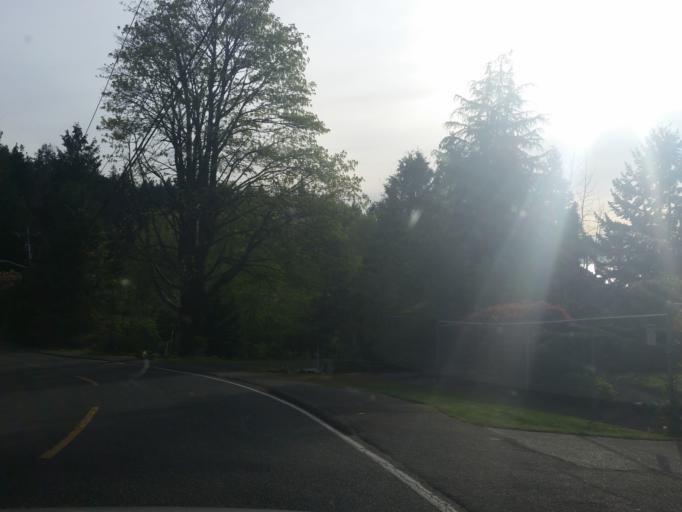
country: US
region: Washington
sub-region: Snohomish County
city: Meadowdale
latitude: 47.8423
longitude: -122.3441
